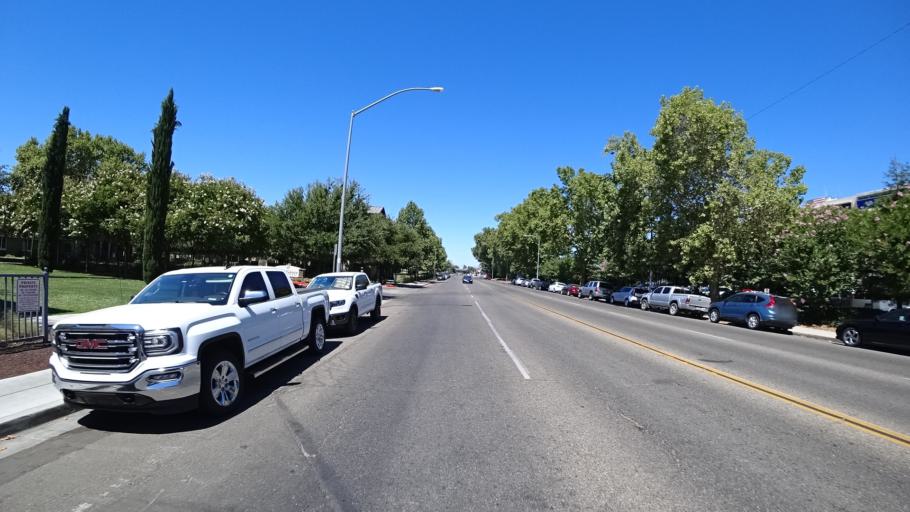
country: US
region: California
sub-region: Fresno County
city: Fresno
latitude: 36.7722
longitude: -119.7788
